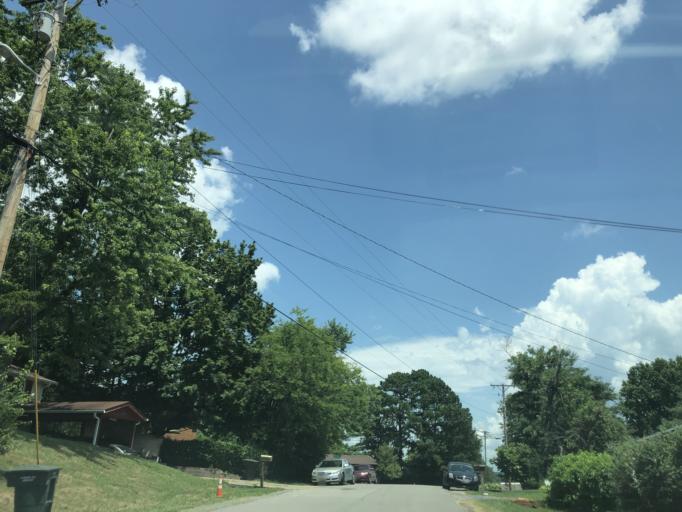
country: US
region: Tennessee
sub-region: Davidson County
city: Lakewood
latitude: 36.1975
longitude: -86.6249
